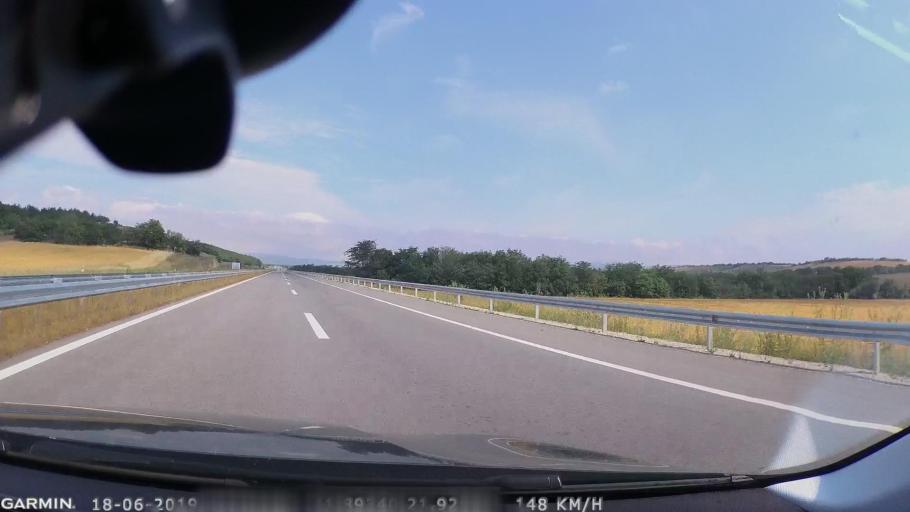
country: MK
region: Sveti Nikole
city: Sveti Nikole
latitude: 41.8944
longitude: 21.9241
